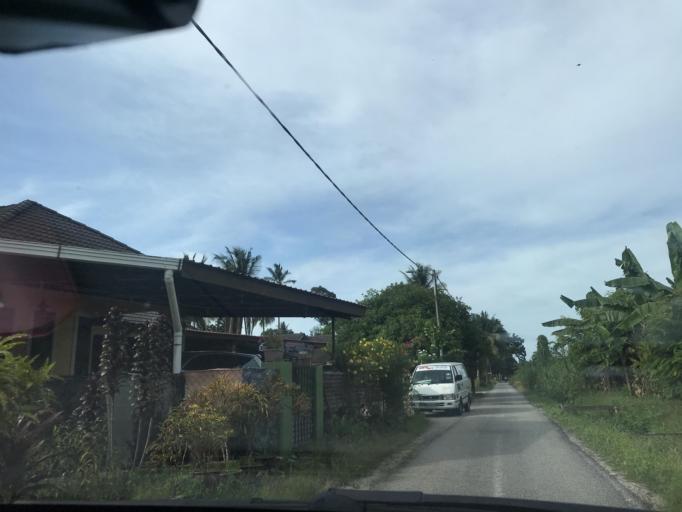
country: MY
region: Kelantan
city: Kota Bharu
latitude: 6.1345
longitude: 102.2191
